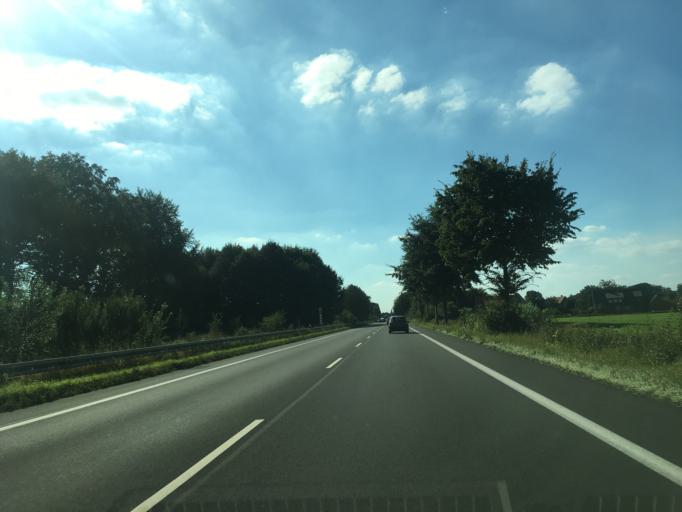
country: DE
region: North Rhine-Westphalia
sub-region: Regierungsbezirk Munster
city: Warendorf
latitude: 51.9474
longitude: 8.0299
